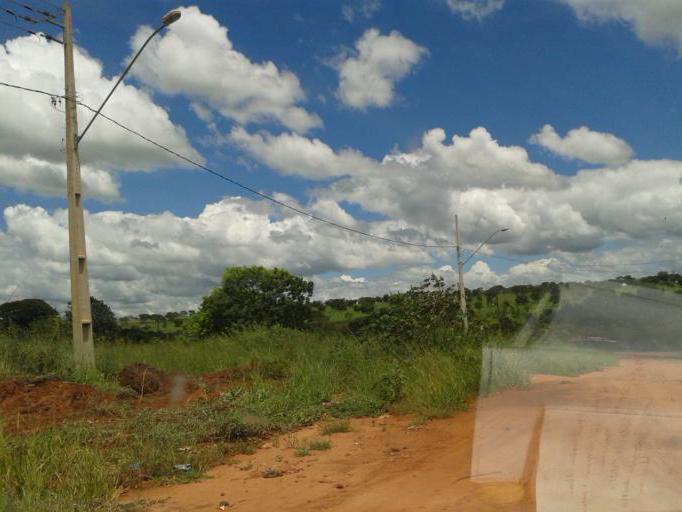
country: BR
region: Minas Gerais
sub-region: Santa Vitoria
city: Santa Vitoria
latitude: -18.8487
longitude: -50.1359
